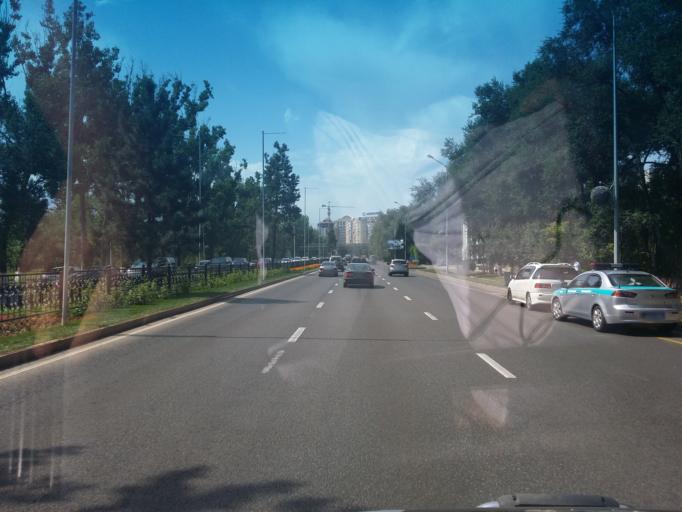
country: KZ
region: Almaty Qalasy
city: Almaty
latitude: 43.2117
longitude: 76.9193
